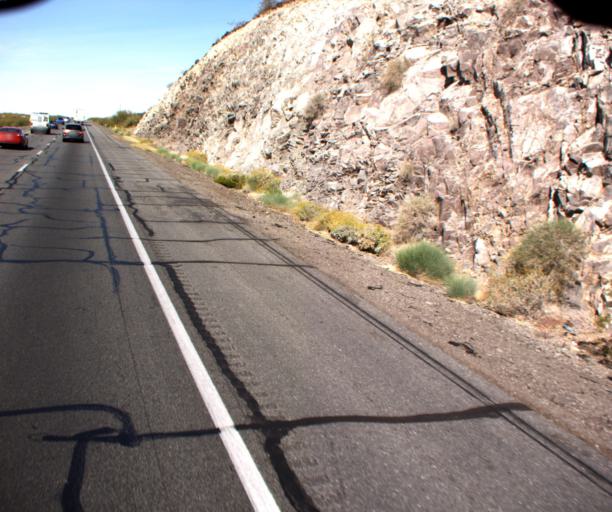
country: US
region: Arizona
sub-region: Maricopa County
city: Buckeye
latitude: 33.5286
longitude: -113.1140
